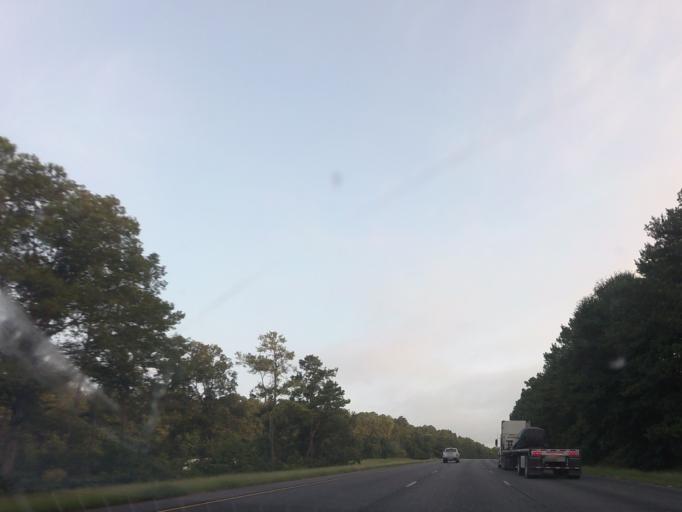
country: US
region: Georgia
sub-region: Monroe County
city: Forsyth
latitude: 33.0933
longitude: -83.9970
